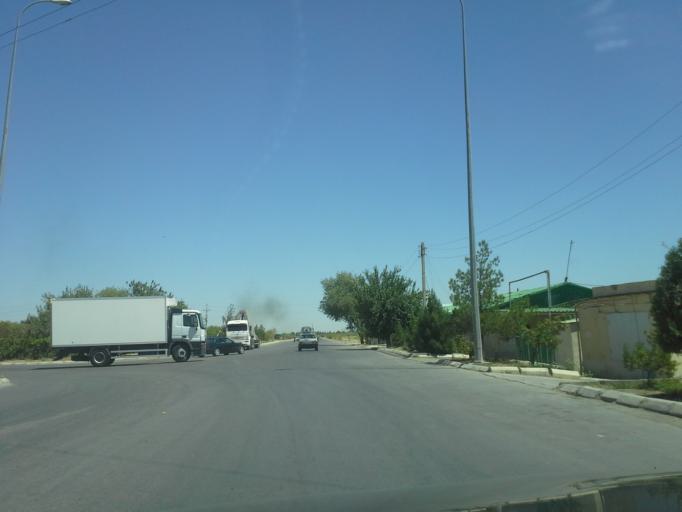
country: TM
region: Ahal
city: Ashgabat
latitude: 38.0085
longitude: 58.3071
